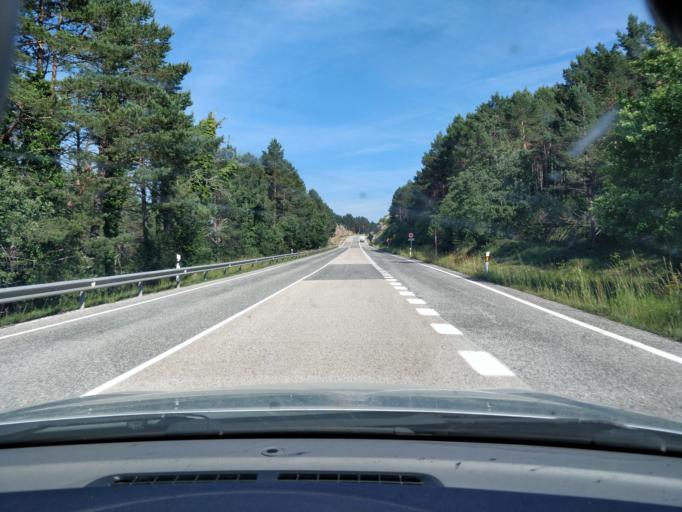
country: ES
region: Cantabria
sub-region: Provincia de Cantabria
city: San Martin de Elines
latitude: 42.9578
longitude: -3.7693
